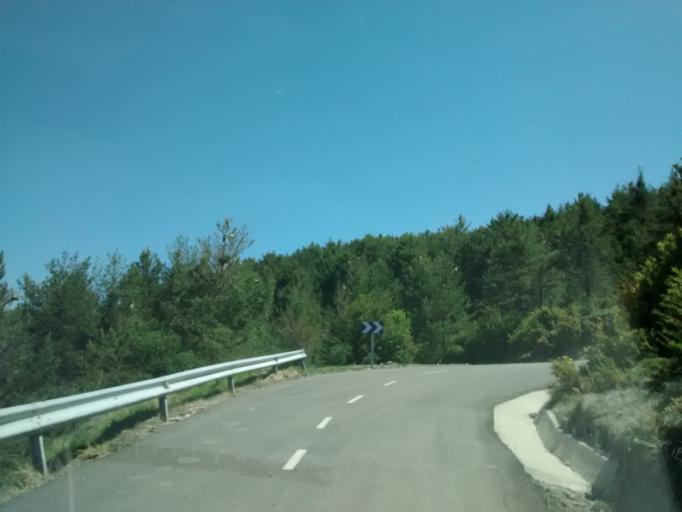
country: ES
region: Aragon
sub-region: Provincia de Huesca
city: Borau
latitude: 42.6657
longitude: -0.5985
